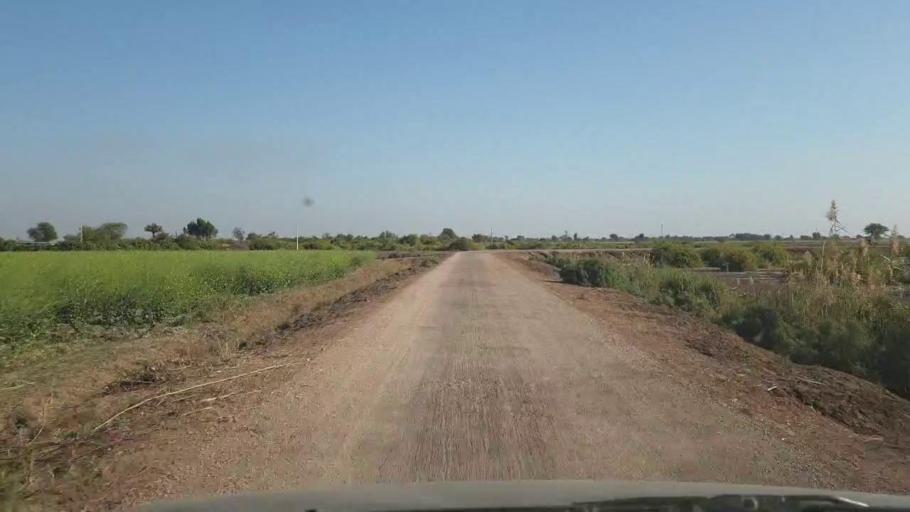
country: PK
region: Sindh
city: Mirwah Gorchani
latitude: 25.3690
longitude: 69.0970
